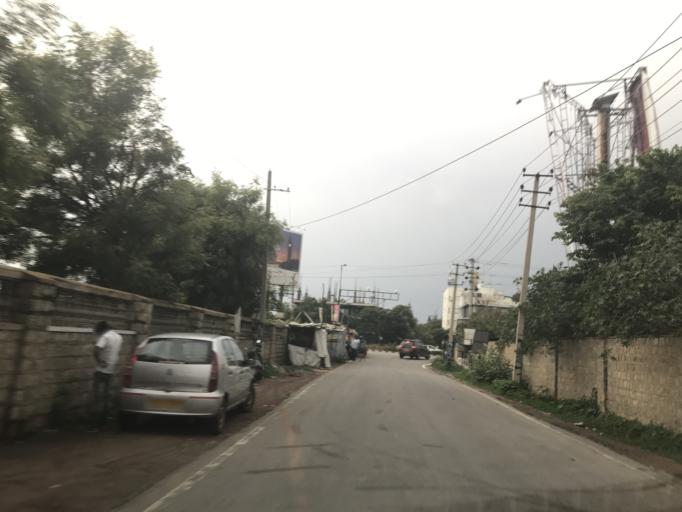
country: IN
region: Karnataka
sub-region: Bangalore Rural
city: Devanhalli
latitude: 13.1895
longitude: 77.6462
